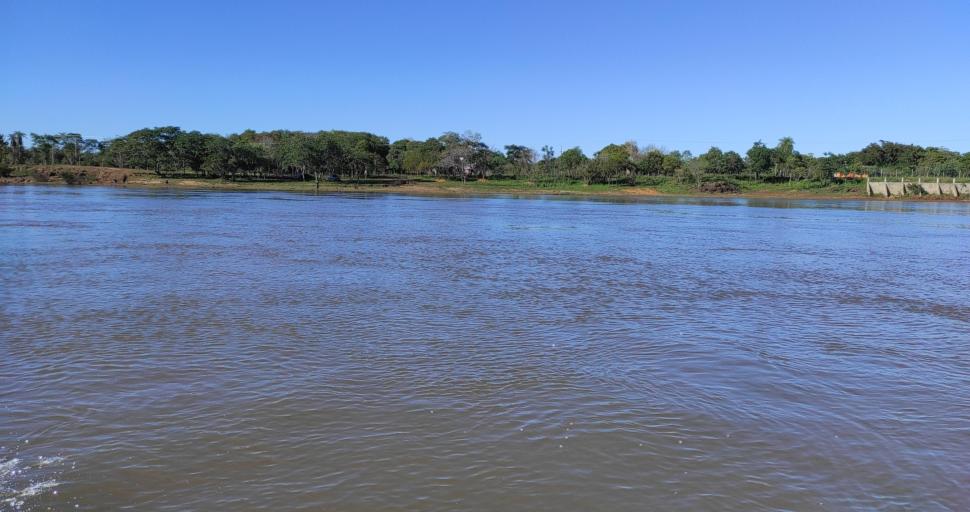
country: AR
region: Corrientes
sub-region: Departamento de Itati
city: Itati
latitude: -27.2633
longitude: -58.2632
